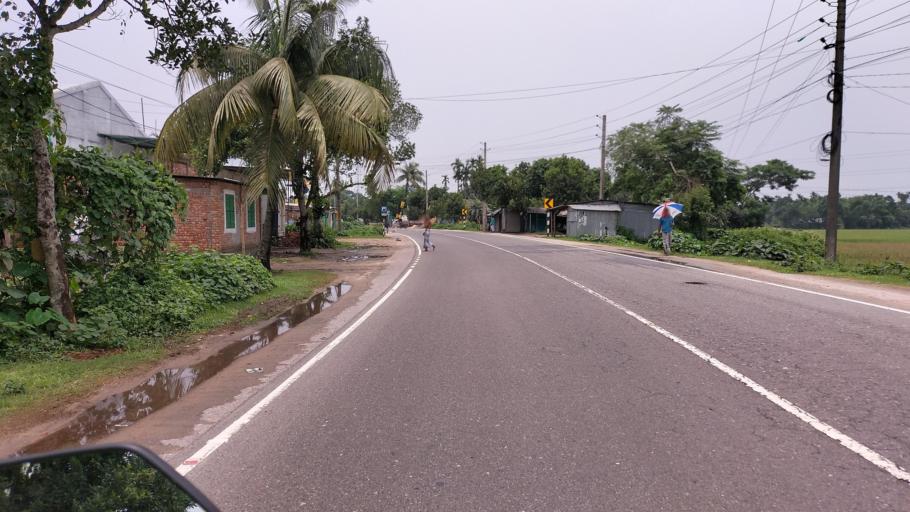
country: BD
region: Dhaka
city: Mymensingh
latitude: 24.7735
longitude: 90.4625
